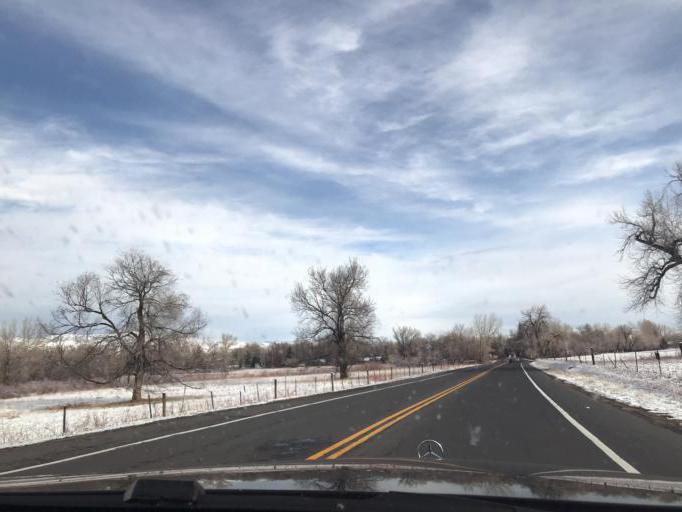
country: US
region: Colorado
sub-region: Boulder County
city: Boulder
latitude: 39.9969
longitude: -105.2127
